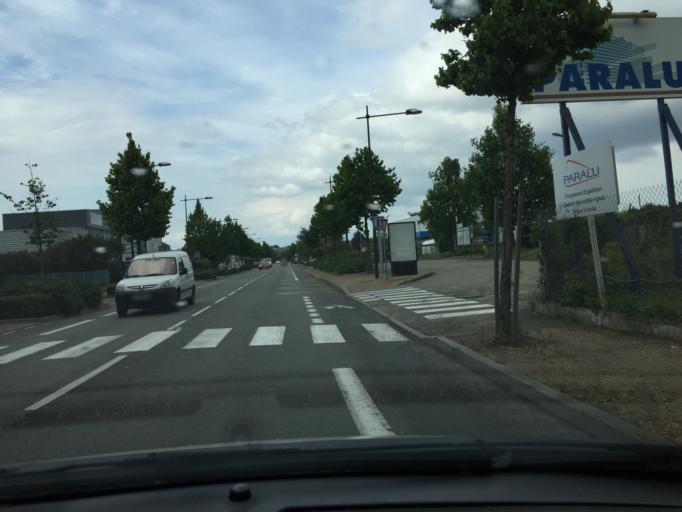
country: FR
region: Rhone-Alpes
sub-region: Departement du Rhone
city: Brignais
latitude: 45.6640
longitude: 4.7522
